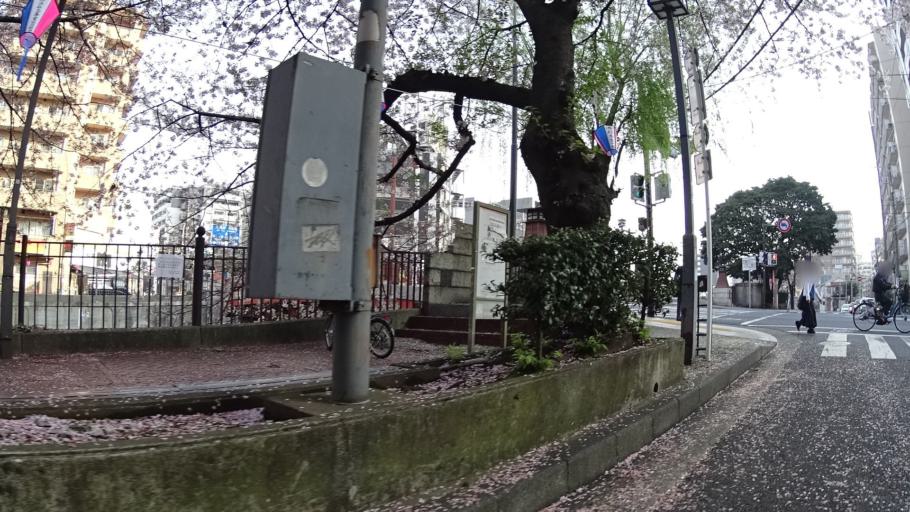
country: JP
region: Kanagawa
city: Yokohama
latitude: 35.4393
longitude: 139.6236
